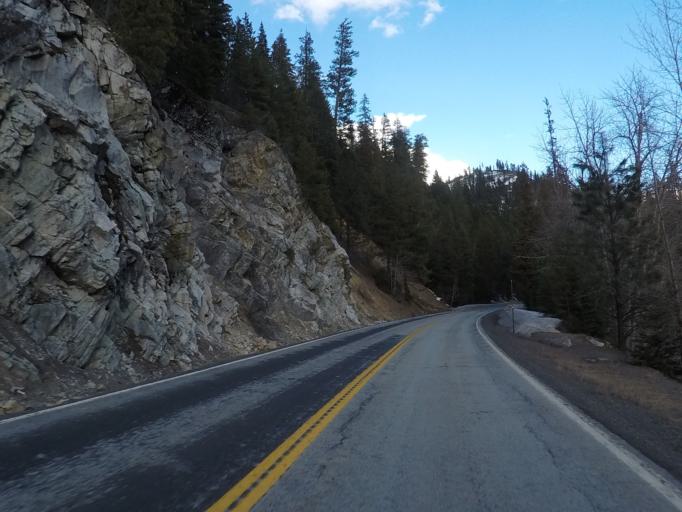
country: US
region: Montana
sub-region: Ravalli County
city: Hamilton
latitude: 46.5175
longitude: -114.7406
